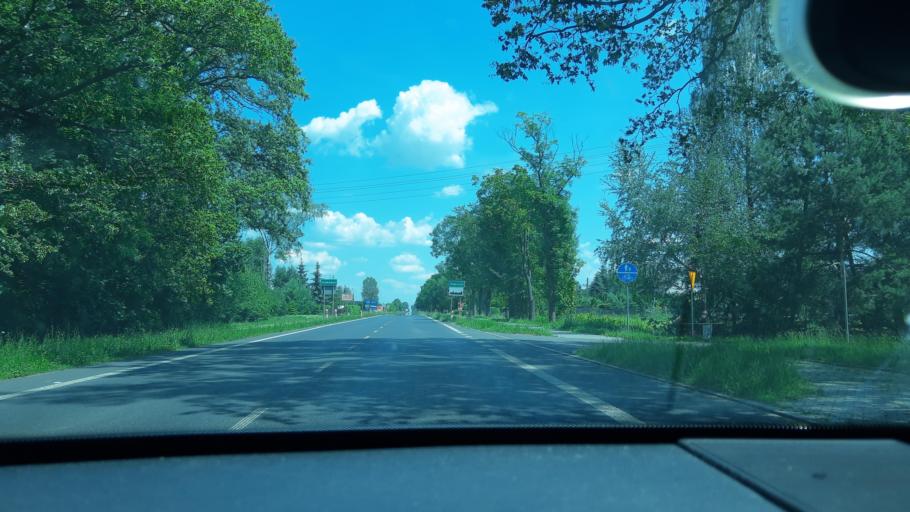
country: PL
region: Lodz Voivodeship
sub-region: Powiat zdunskowolski
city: Zapolice
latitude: 51.6042
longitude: 18.8331
